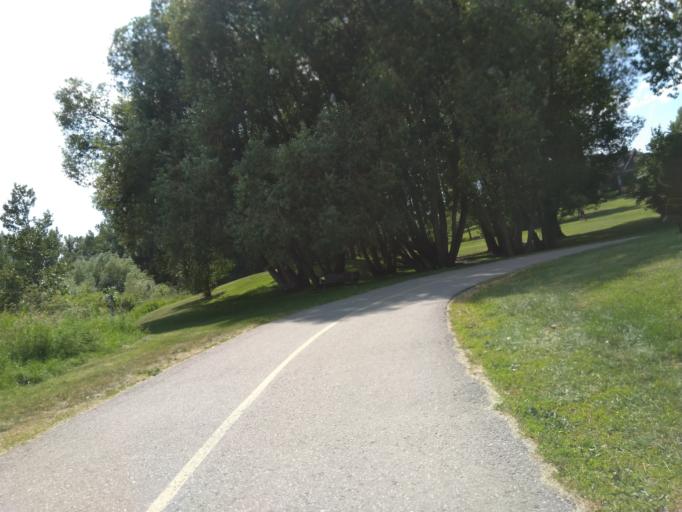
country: CA
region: Alberta
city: Calgary
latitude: 51.0741
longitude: -114.0882
